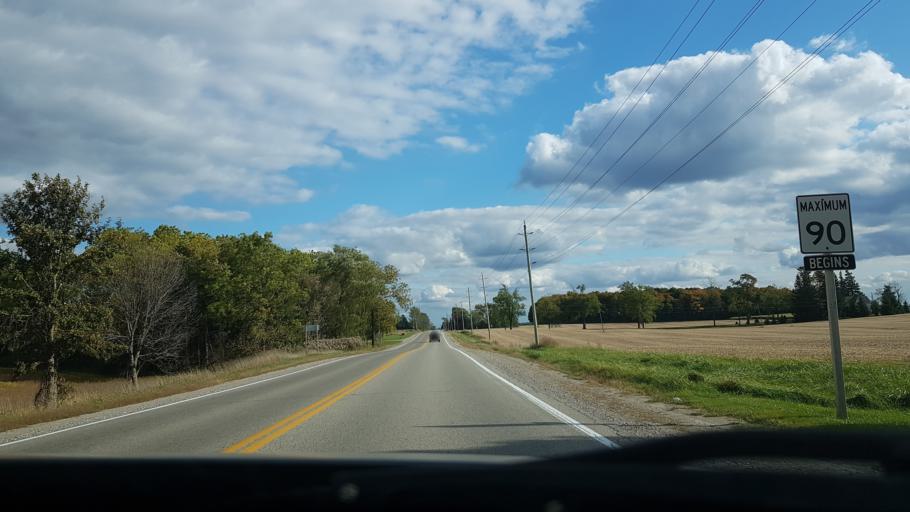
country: CA
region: Ontario
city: Delaware
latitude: 43.0282
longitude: -81.4598
